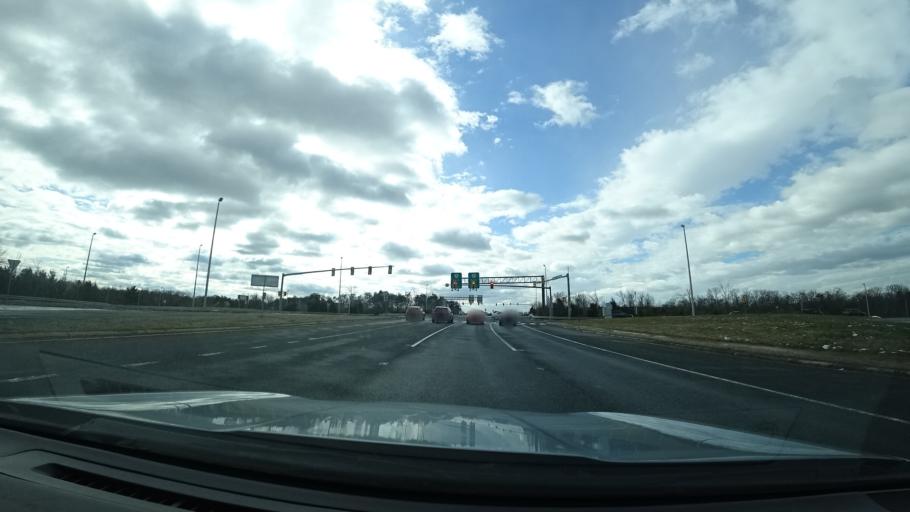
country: US
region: Virginia
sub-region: Fairfax County
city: Dranesville
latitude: 39.0117
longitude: -77.3633
